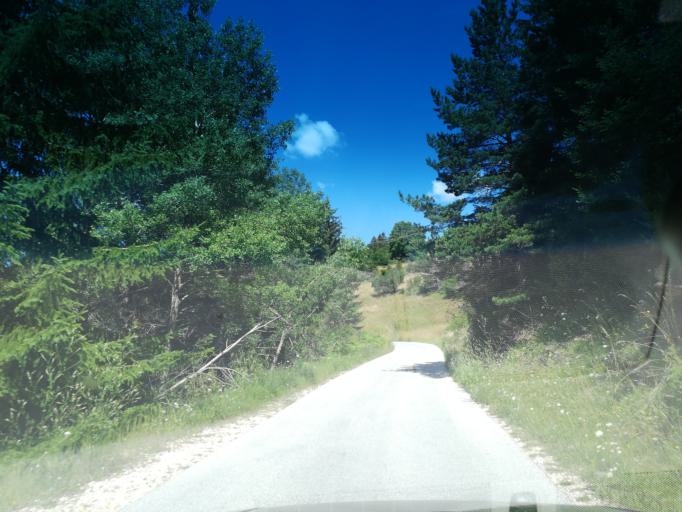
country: BG
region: Smolyan
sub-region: Obshtina Chepelare
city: Chepelare
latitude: 41.6697
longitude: 24.7864
